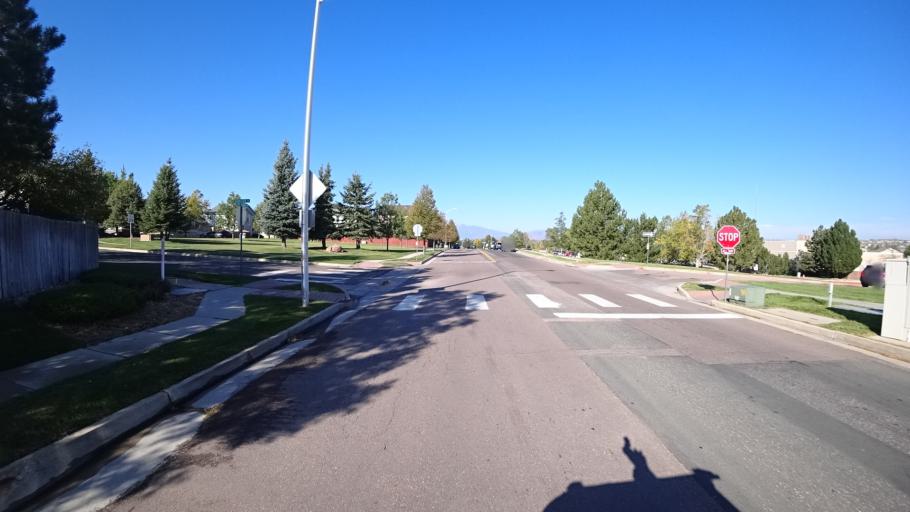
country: US
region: Colorado
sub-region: El Paso County
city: Cimarron Hills
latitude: 38.8775
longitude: -104.6985
